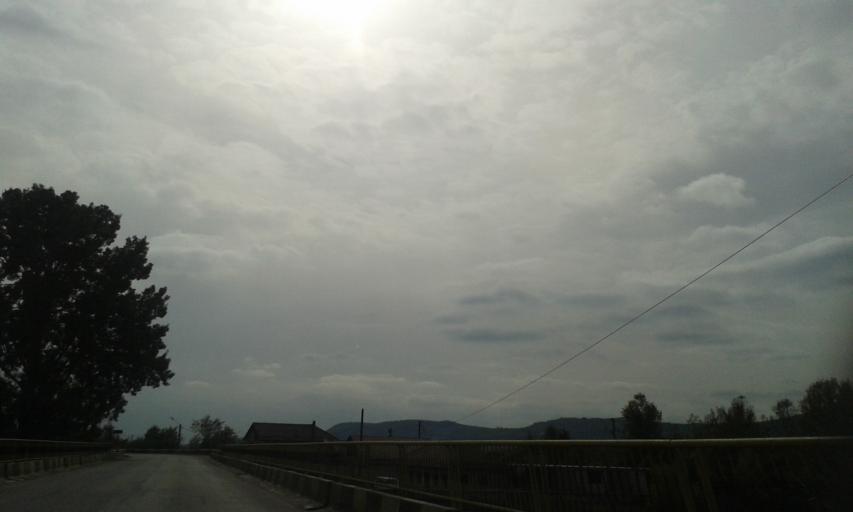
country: RO
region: Gorj
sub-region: Comuna Targu Carbunesti
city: Targu Carbunesti
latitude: 44.9486
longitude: 23.5124
